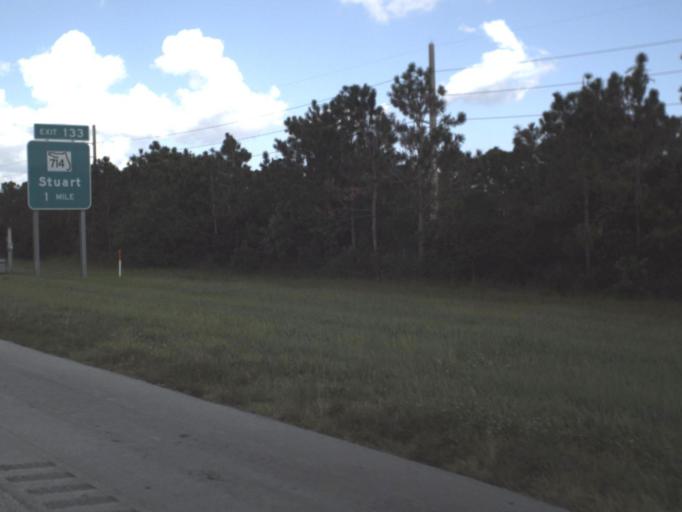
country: US
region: Florida
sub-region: Martin County
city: Palm City
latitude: 27.1439
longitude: -80.2927
